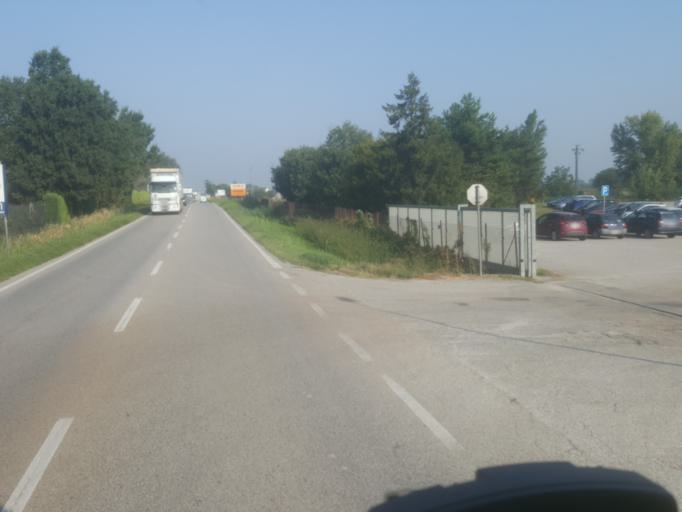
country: IT
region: Emilia-Romagna
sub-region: Provincia di Ravenna
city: Fornace Zarattini
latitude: 44.4336
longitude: 12.1475
